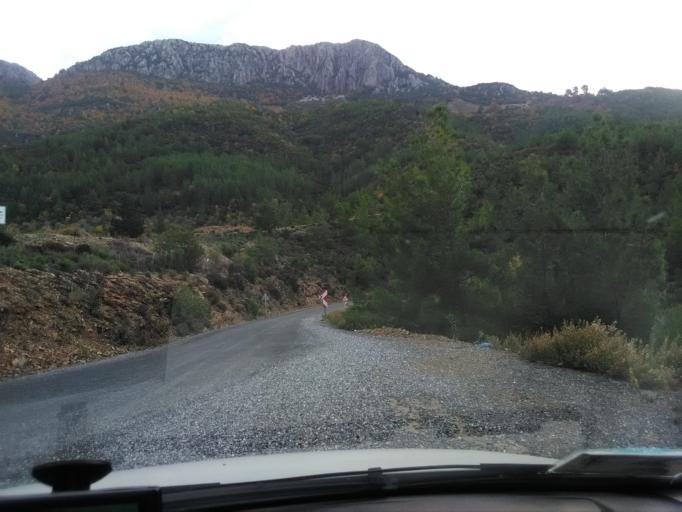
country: TR
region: Antalya
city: Gazipasa
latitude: 36.3060
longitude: 32.3987
